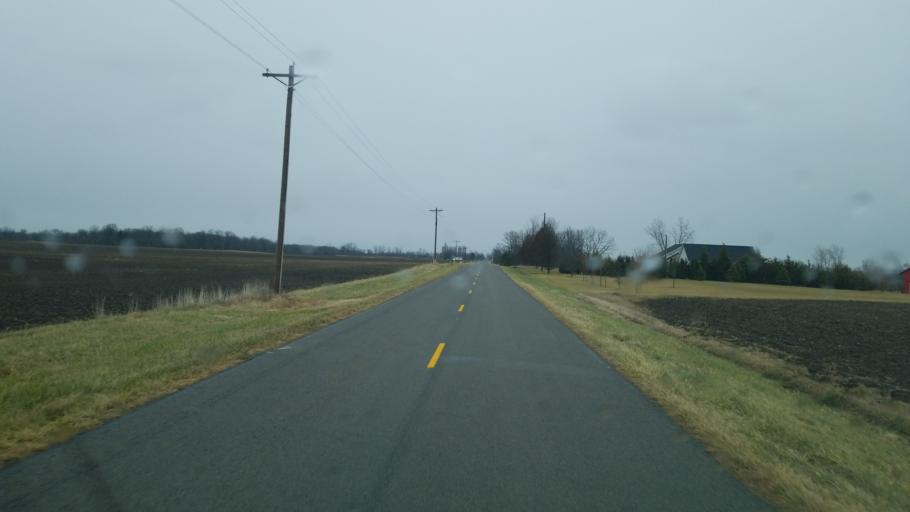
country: US
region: Ohio
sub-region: Logan County
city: Northwood
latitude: 40.4514
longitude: -83.5741
